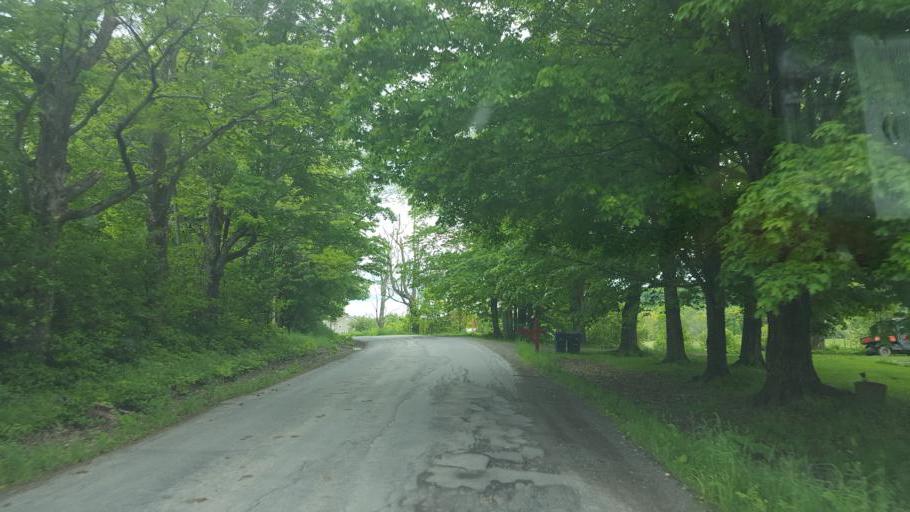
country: US
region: New York
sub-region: Otsego County
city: Richfield Springs
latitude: 42.8600
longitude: -75.0799
